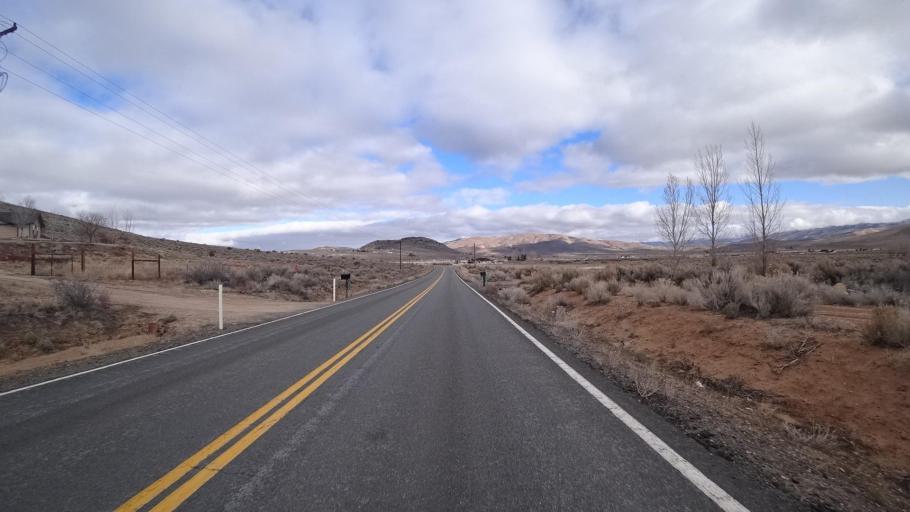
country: US
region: Nevada
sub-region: Washoe County
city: Cold Springs
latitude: 39.8581
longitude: -119.9353
